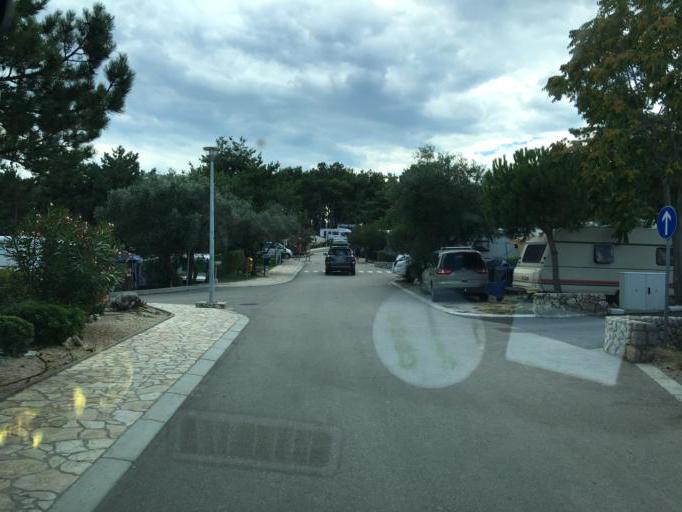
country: HR
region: Primorsko-Goranska
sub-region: Grad Krk
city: Krk
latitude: 45.0200
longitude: 14.5707
